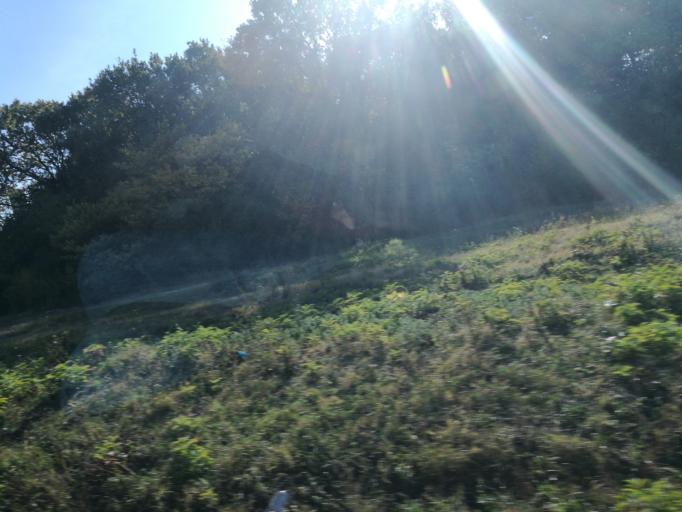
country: RO
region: Ilfov
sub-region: Comuna Dragomiresti-Vale
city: Dragomiresti-Vale
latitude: 44.4722
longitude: 25.9143
